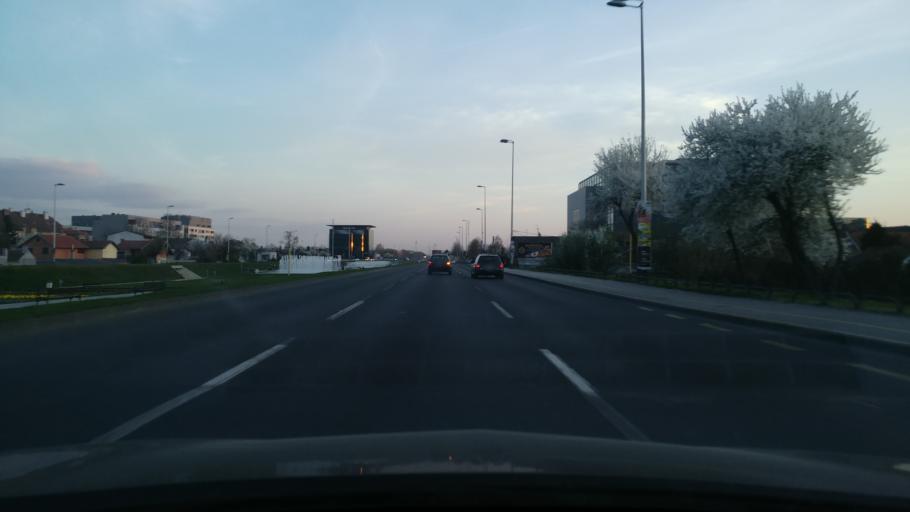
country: HR
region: Grad Zagreb
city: Zagreb - Centar
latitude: 45.7992
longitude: 15.9787
